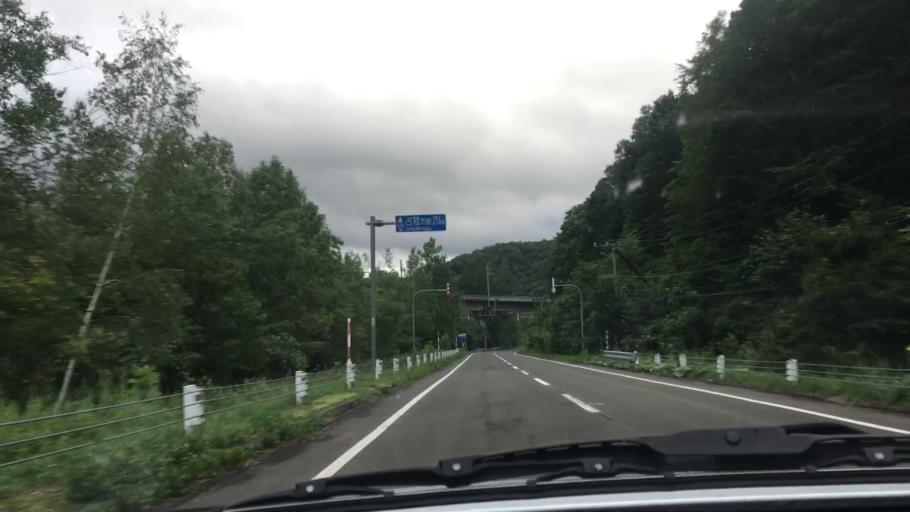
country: JP
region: Hokkaido
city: Shimo-furano
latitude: 43.0641
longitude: 142.5316
